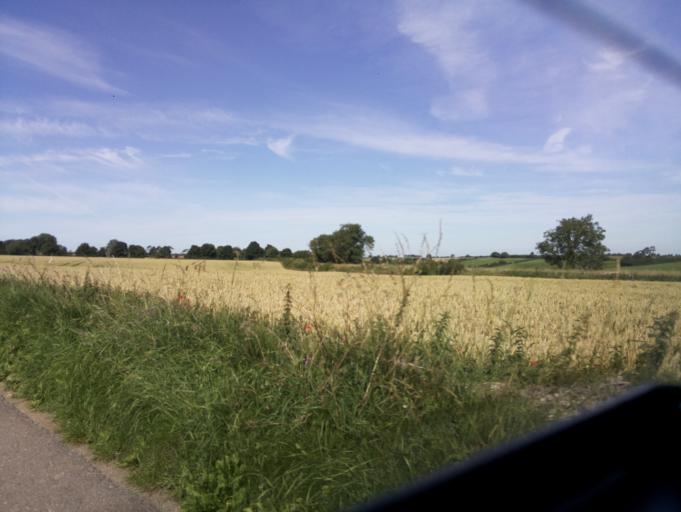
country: GB
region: England
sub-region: South Gloucestershire
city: Cold Ashton
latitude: 51.4564
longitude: -2.3515
